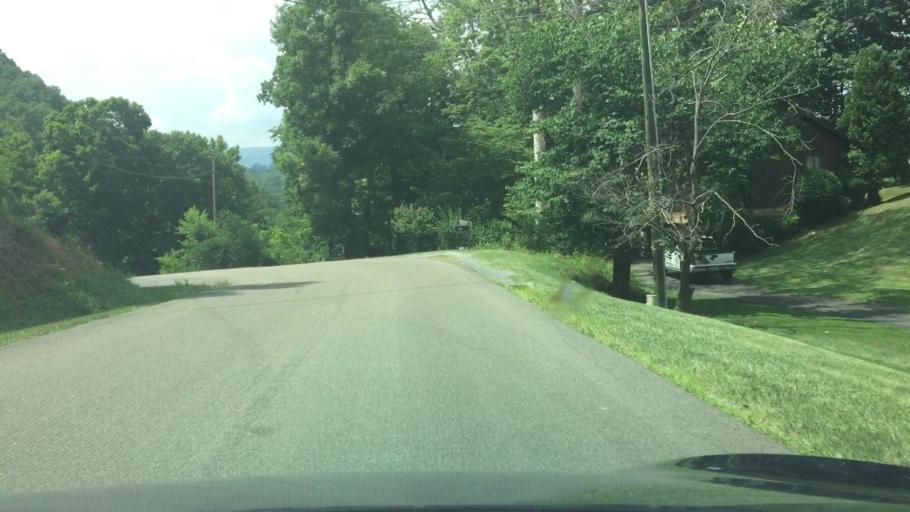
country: US
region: Virginia
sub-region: Wythe County
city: Wytheville
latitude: 36.9288
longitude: -81.0664
